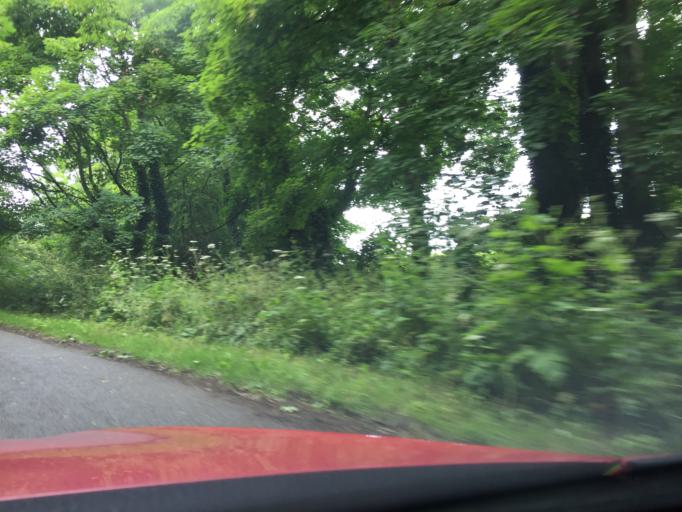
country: GB
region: England
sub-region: Northamptonshire
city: Daventry
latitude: 52.2346
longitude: -1.1506
